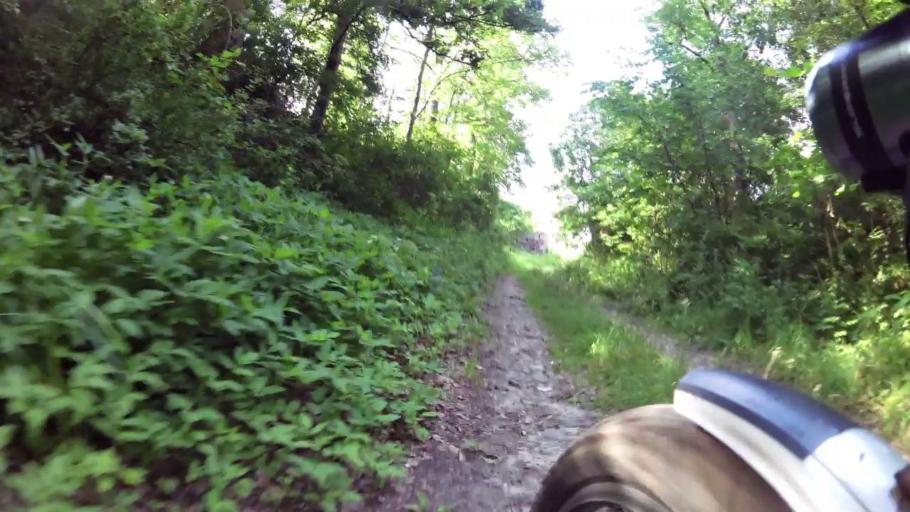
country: PL
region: West Pomeranian Voivodeship
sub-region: Powiat lobeski
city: Wegorzyno
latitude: 53.5405
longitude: 15.4564
